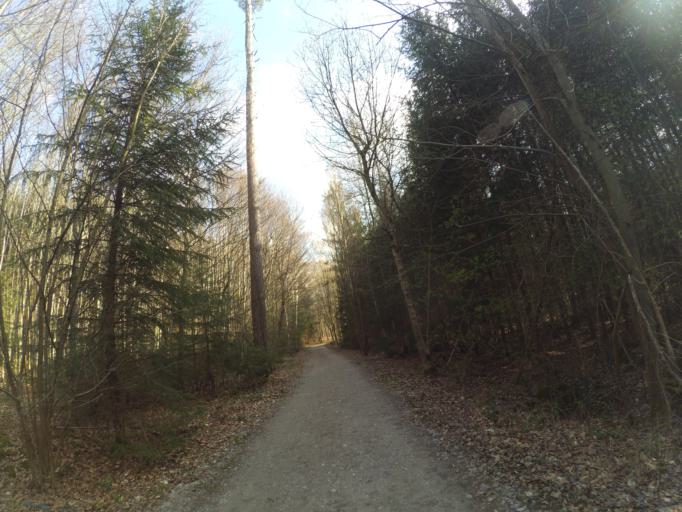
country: DE
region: Bavaria
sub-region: Swabia
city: Bad Worishofen
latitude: 48.0105
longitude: 10.5730
